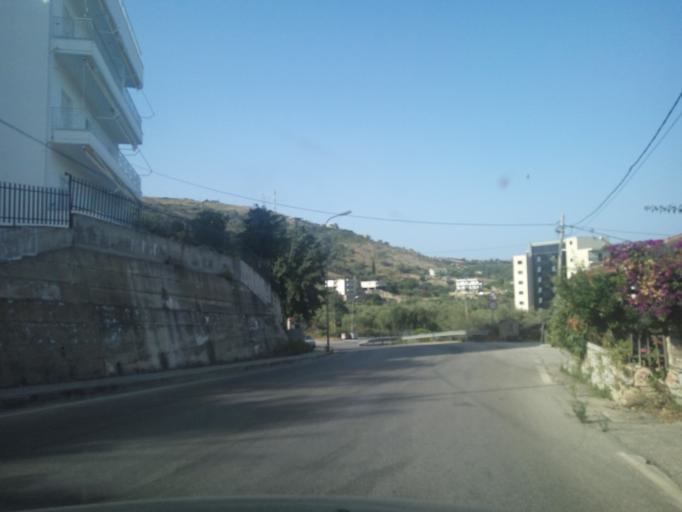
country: AL
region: Vlore
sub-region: Rrethi i Vlores
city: Himare
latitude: 40.0947
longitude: 19.7591
